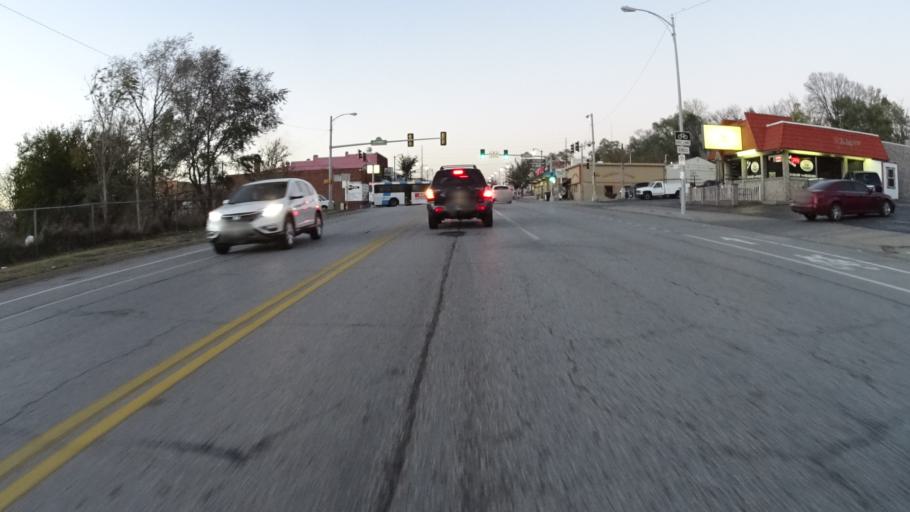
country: US
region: Nebraska
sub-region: Douglas County
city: Omaha
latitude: 41.2050
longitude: -95.9471
